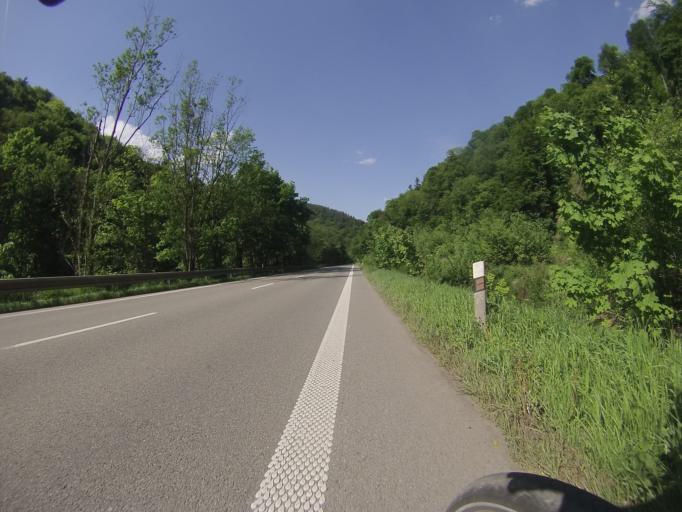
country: CZ
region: South Moravian
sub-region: Okres Blansko
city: Adamov
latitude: 49.3301
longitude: 16.6438
